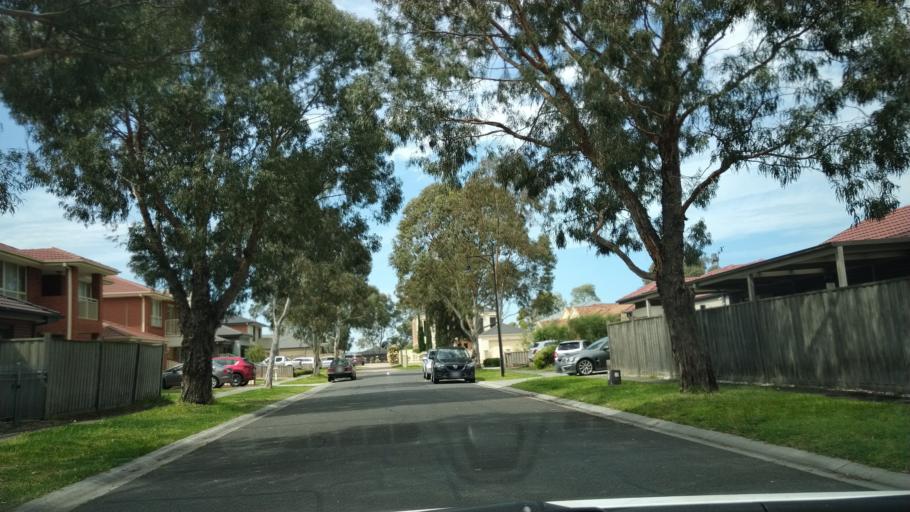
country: AU
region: Victoria
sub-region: Greater Dandenong
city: Keysborough
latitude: -37.9990
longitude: 145.1603
